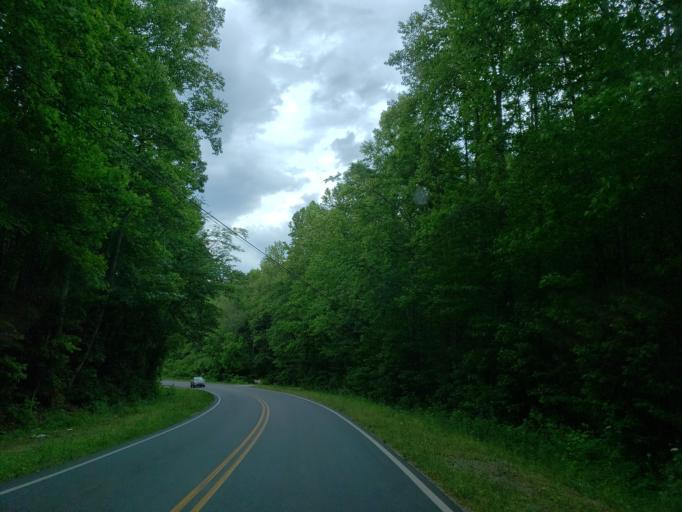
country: US
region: Georgia
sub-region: Polk County
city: Rockmart
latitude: 33.9583
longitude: -85.0462
